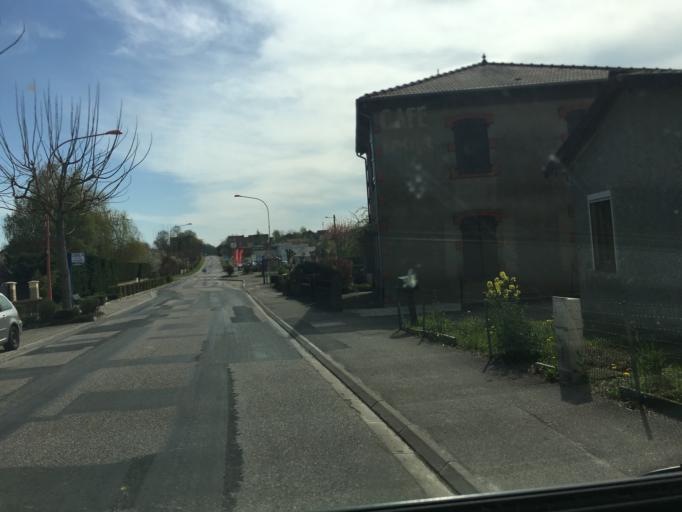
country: FR
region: Lorraine
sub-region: Departement de la Meuse
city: Lerouville
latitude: 48.7892
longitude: 5.5502
